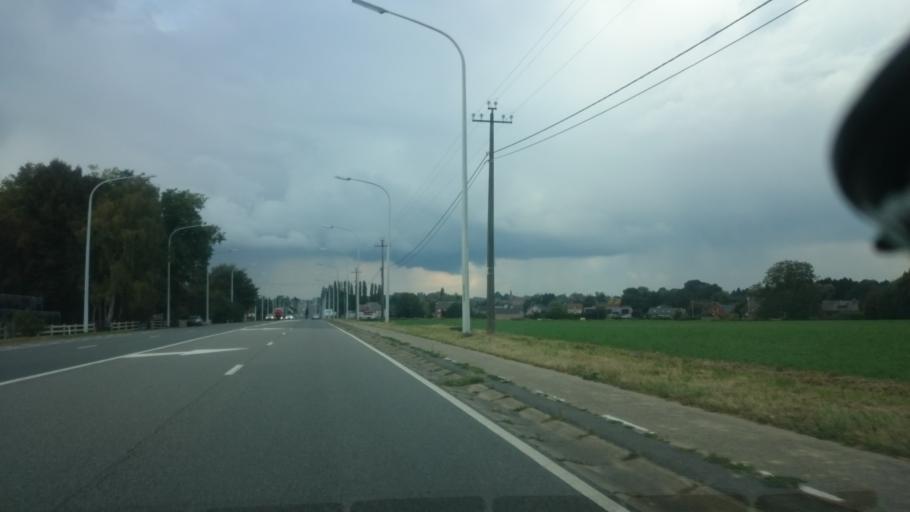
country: BE
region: Wallonia
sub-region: Province de Namur
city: Gembloux
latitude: 50.5272
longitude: 4.7509
